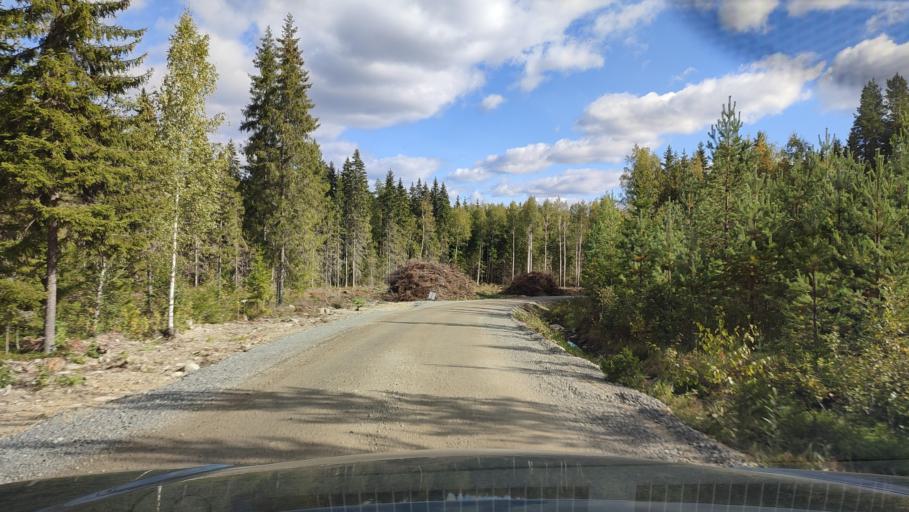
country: FI
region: Southern Ostrobothnia
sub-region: Suupohja
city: Karijoki
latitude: 62.2044
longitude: 21.5926
